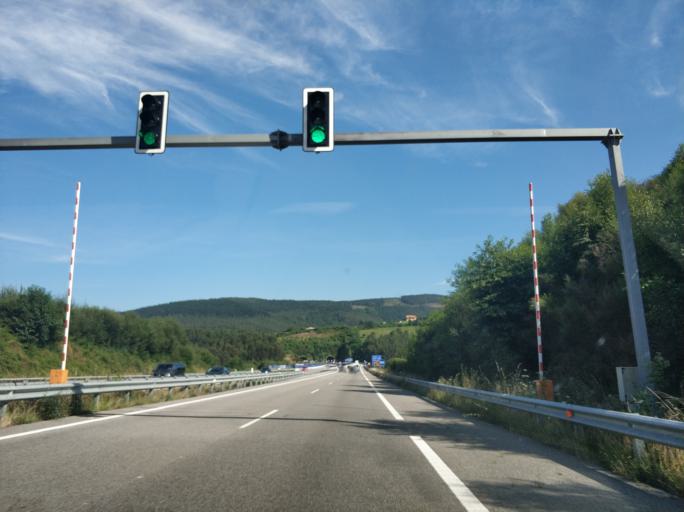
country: ES
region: Asturias
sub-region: Province of Asturias
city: Cudillero
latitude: 43.5472
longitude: -6.1612
